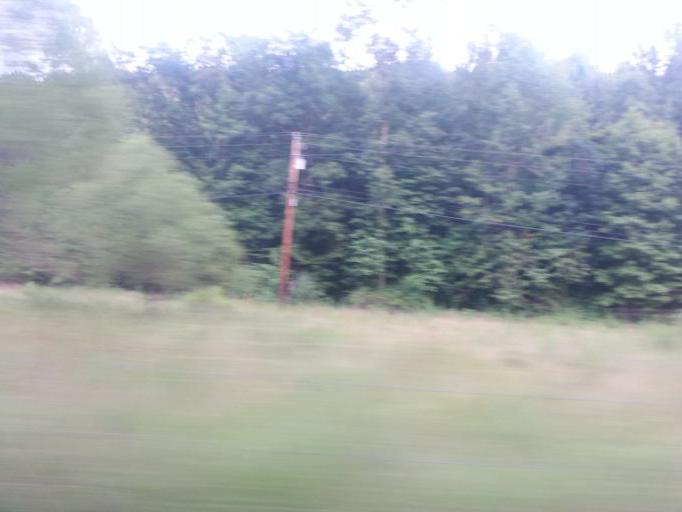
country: US
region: Tennessee
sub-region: Anderson County
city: Rocky Top
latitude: 36.1523
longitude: -84.2027
